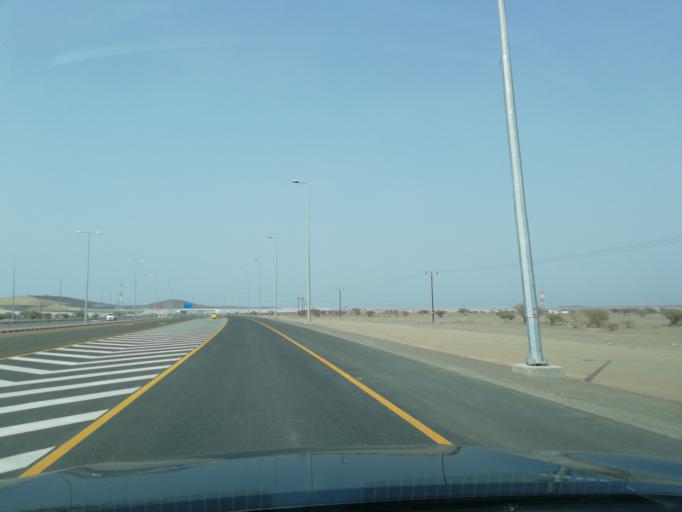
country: OM
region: Al Batinah
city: Al Liwa'
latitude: 24.3784
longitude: 56.5423
